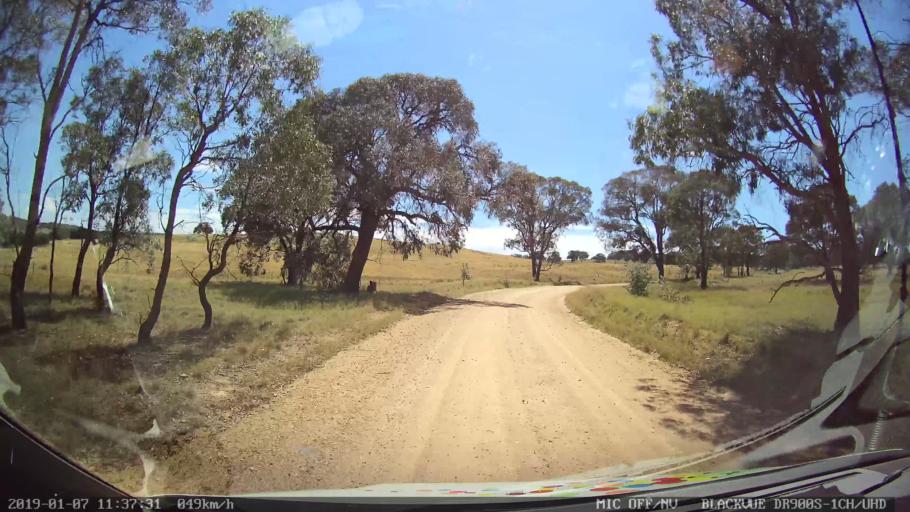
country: AU
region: New South Wales
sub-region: Armidale Dumaresq
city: Armidale
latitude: -30.3705
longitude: 151.5661
